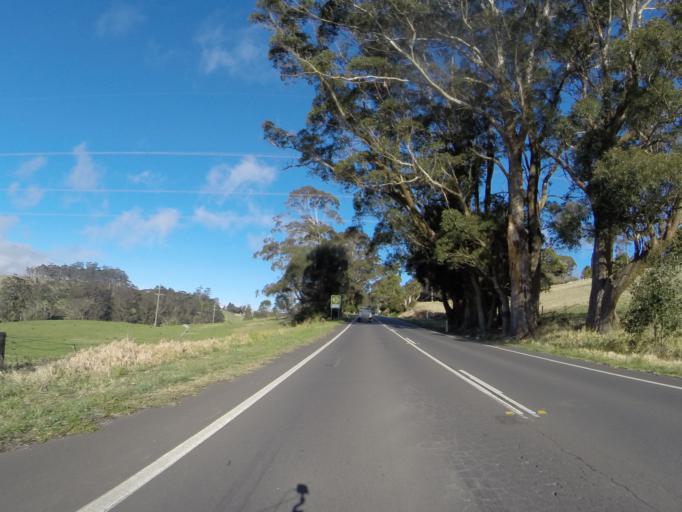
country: AU
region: New South Wales
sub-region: Shoalhaven Shire
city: Kangaroo Valley
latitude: -34.5865
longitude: 150.5393
